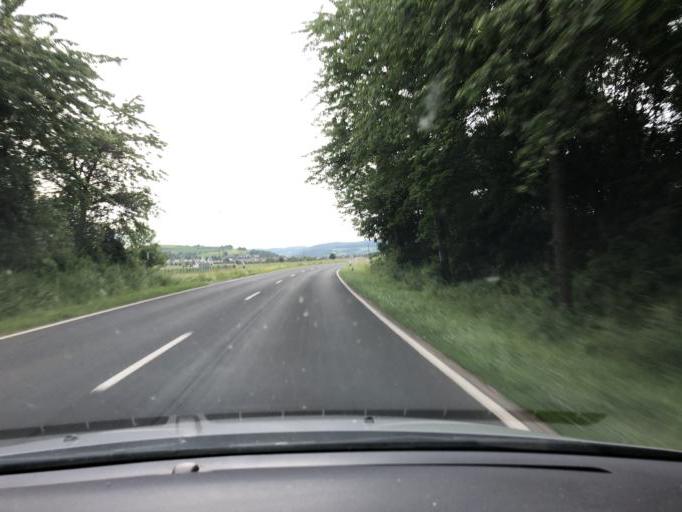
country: DE
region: Hesse
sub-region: Regierungsbezirk Kassel
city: Alheim
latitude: 51.0080
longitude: 9.6872
